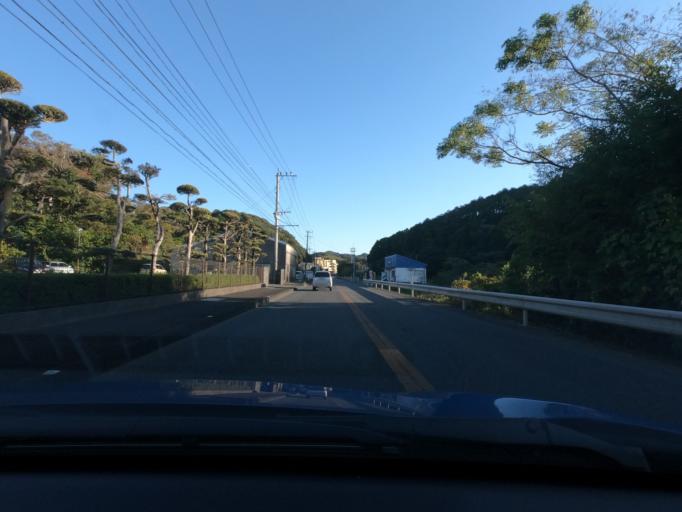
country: JP
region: Kagoshima
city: Satsumasendai
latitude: 31.8632
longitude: 130.2263
